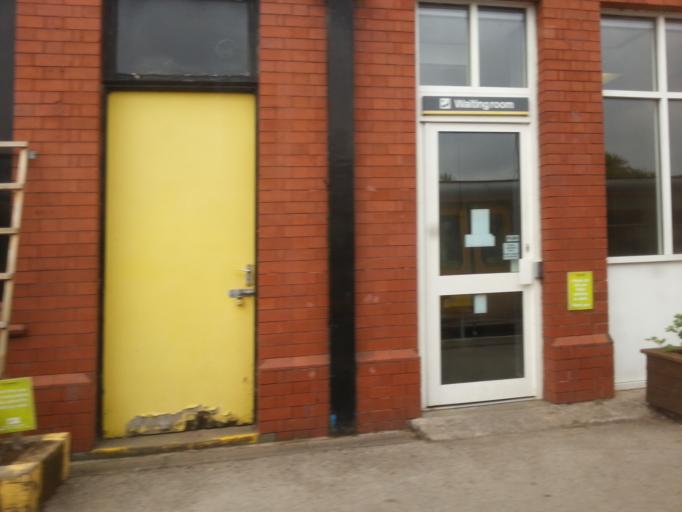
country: GB
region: England
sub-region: Sefton
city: Formby
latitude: 53.5538
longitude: -3.0709
